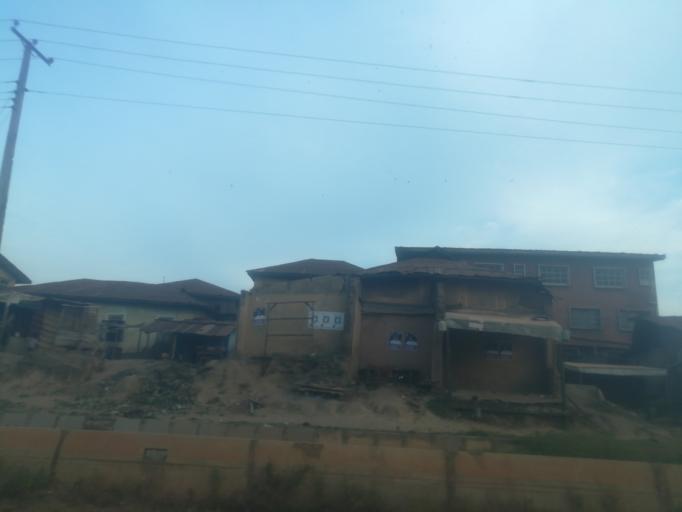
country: NG
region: Ogun
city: Abeokuta
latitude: 7.1706
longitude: 3.3383
